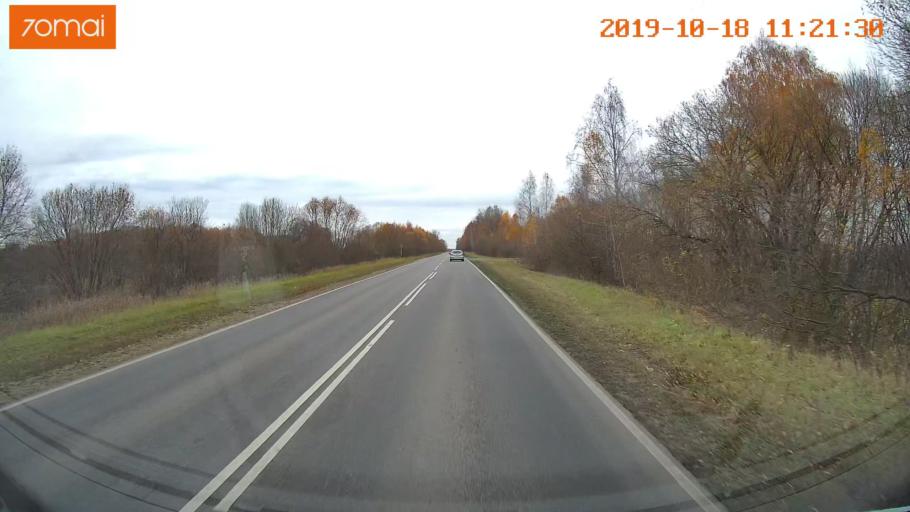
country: RU
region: Tula
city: Kimovsk
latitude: 54.0748
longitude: 38.5660
